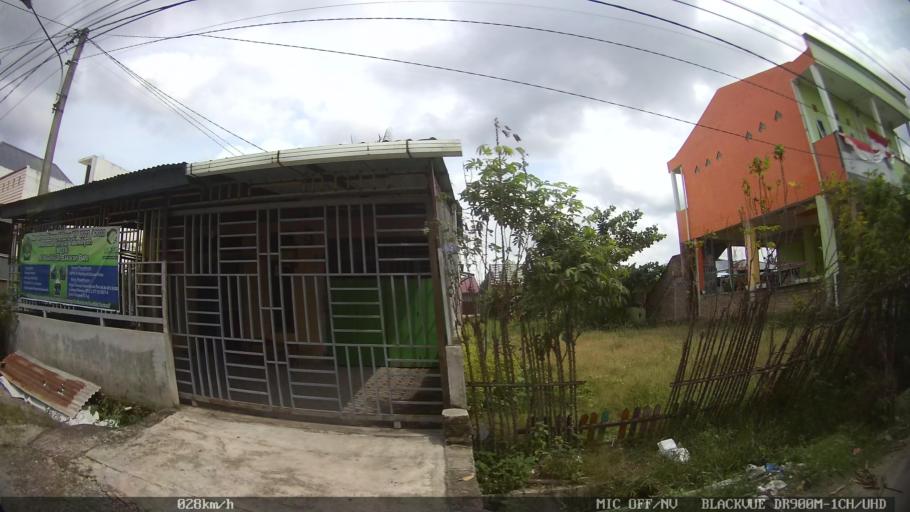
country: ID
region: North Sumatra
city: Percut
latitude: 3.5713
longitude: 98.8664
